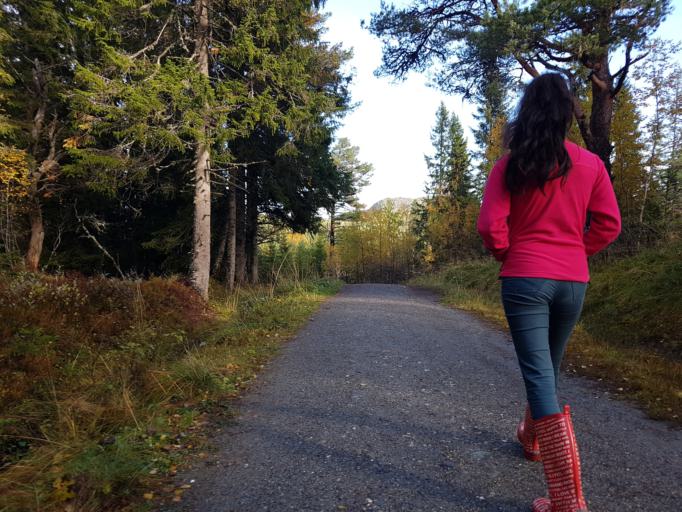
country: NO
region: Sor-Trondelag
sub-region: Trondheim
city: Trondheim
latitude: 63.4194
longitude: 10.2825
